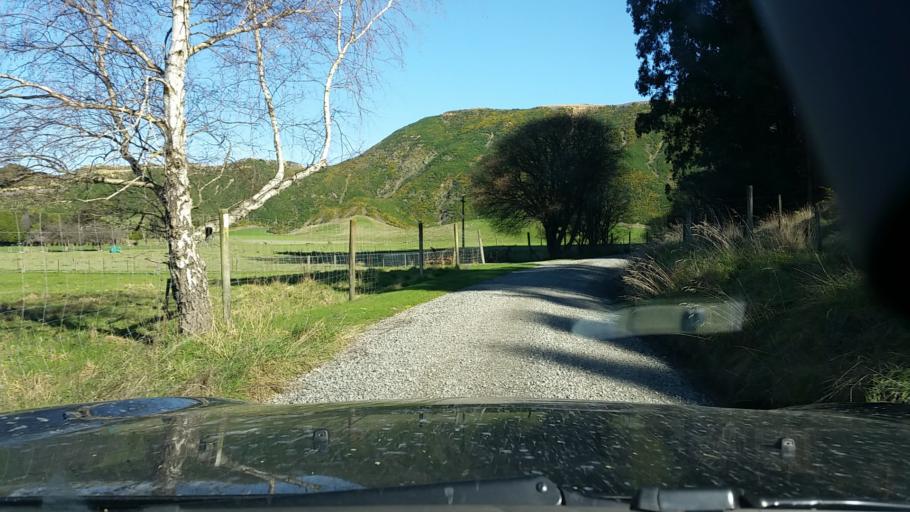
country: NZ
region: Marlborough
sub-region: Marlborough District
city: Blenheim
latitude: -41.4630
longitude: 173.7965
